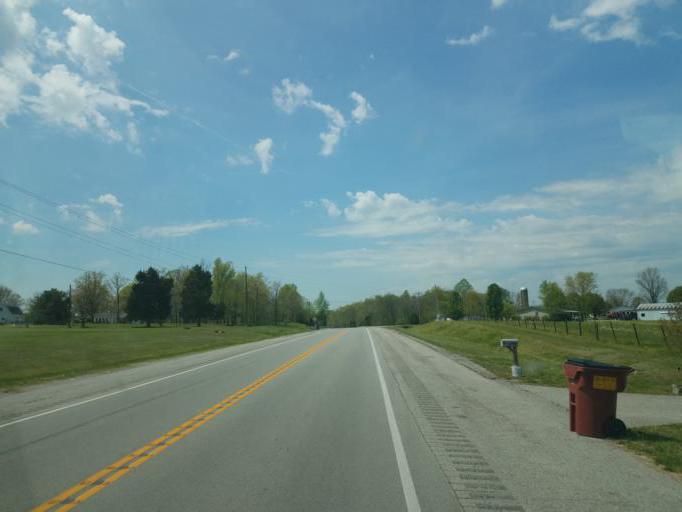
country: US
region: Kentucky
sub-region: Warren County
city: Bowling Green
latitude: 37.0939
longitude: -86.4421
